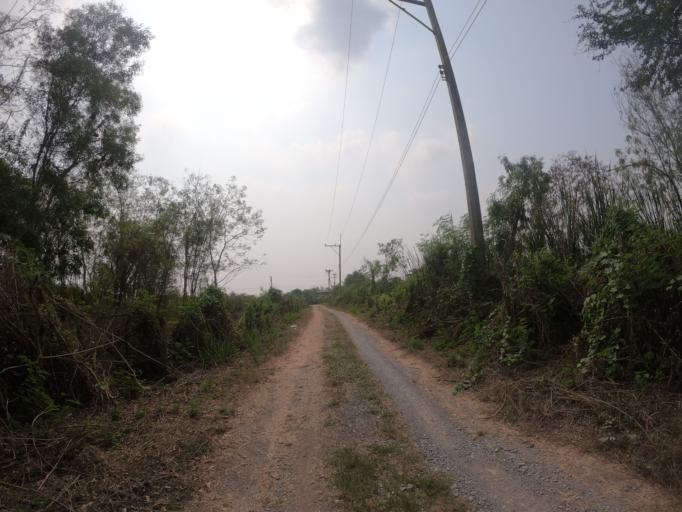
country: TH
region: Pathum Thani
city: Nong Suea
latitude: 14.0672
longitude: 100.8496
